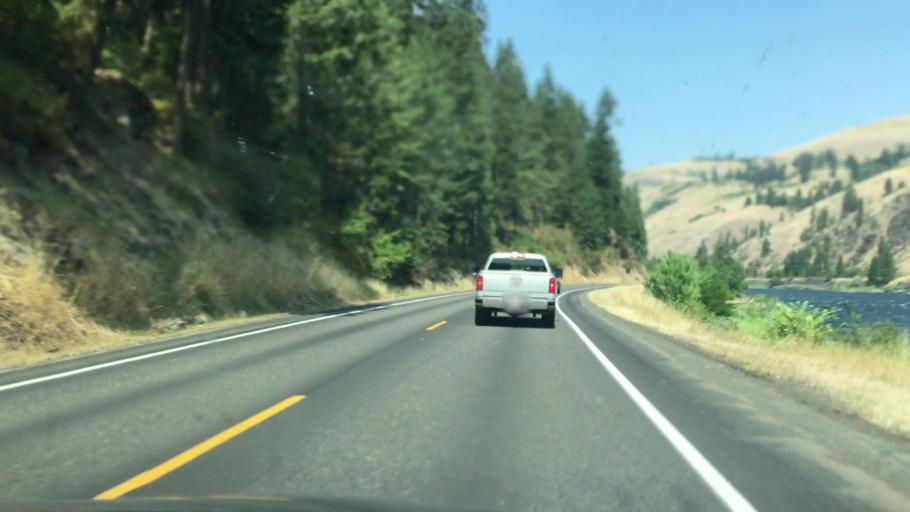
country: US
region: Idaho
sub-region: Clearwater County
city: Orofino
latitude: 46.4912
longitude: -116.4581
